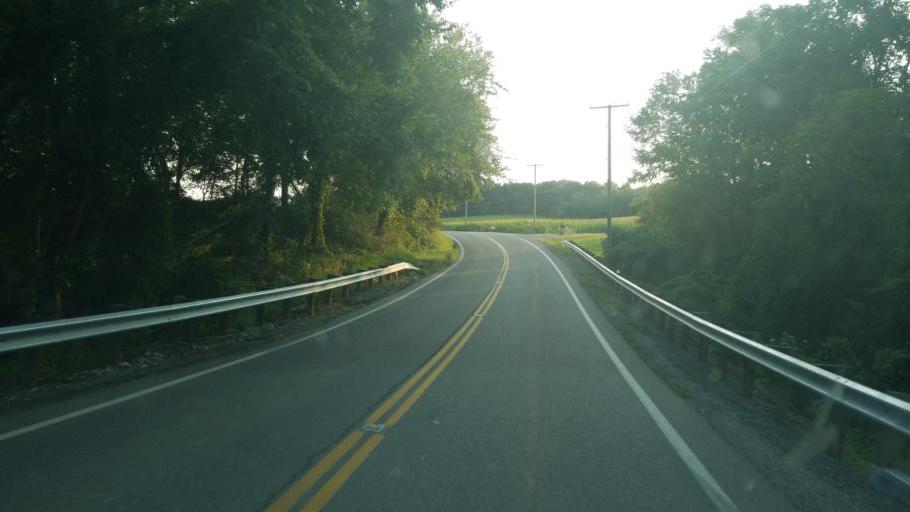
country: US
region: Ohio
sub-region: Wayne County
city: Shreve
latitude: 40.6650
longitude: -82.1165
